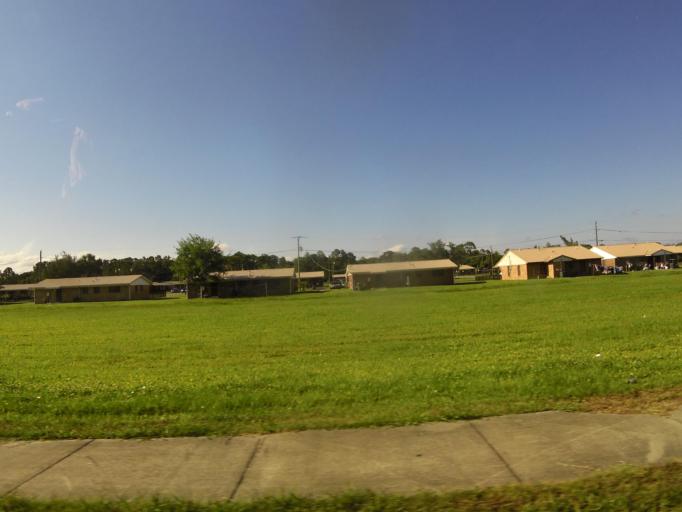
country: US
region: Florida
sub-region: Putnam County
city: Palatka
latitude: 29.6528
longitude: -81.6515
